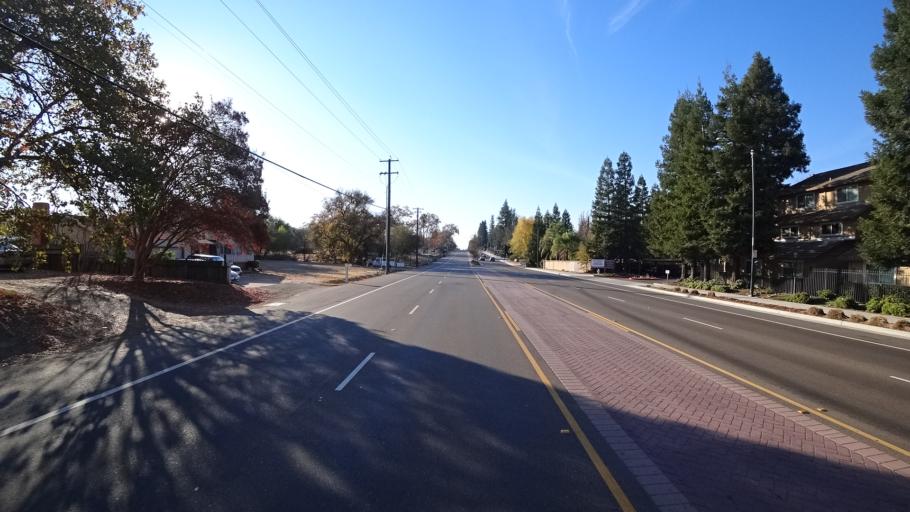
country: US
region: California
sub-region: Sacramento County
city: Citrus Heights
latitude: 38.7170
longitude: -121.2717
